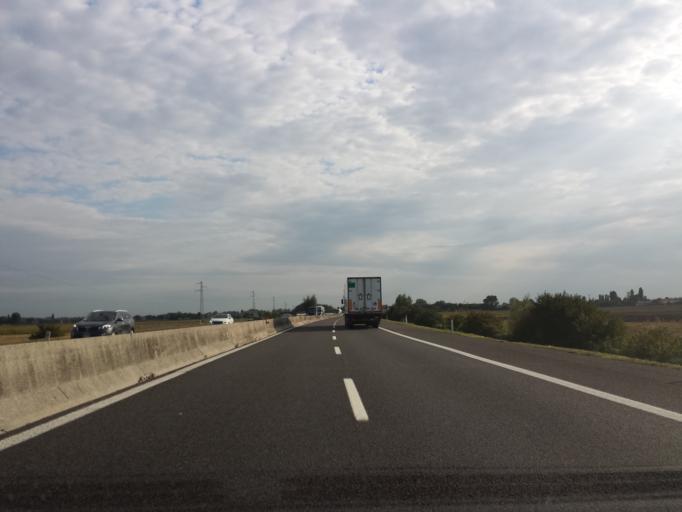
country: IT
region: Veneto
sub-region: Provincia di Padova
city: Stanghella
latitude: 45.1354
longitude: 11.7749
